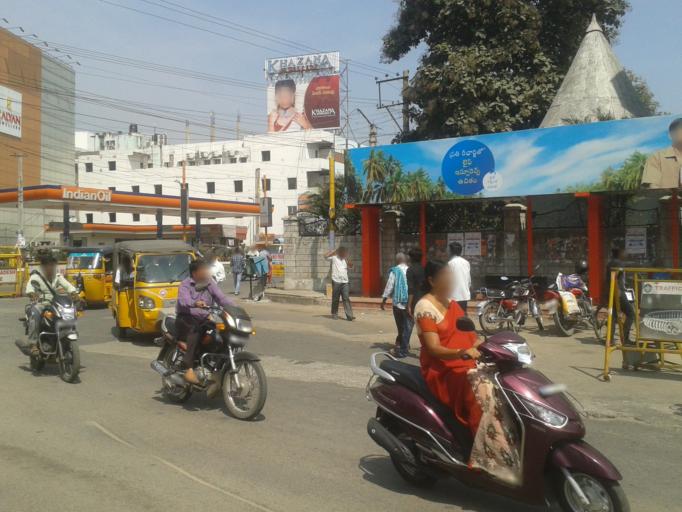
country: IN
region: Andhra Pradesh
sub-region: Chittoor
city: Tirupati
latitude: 13.6360
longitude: 79.4223
